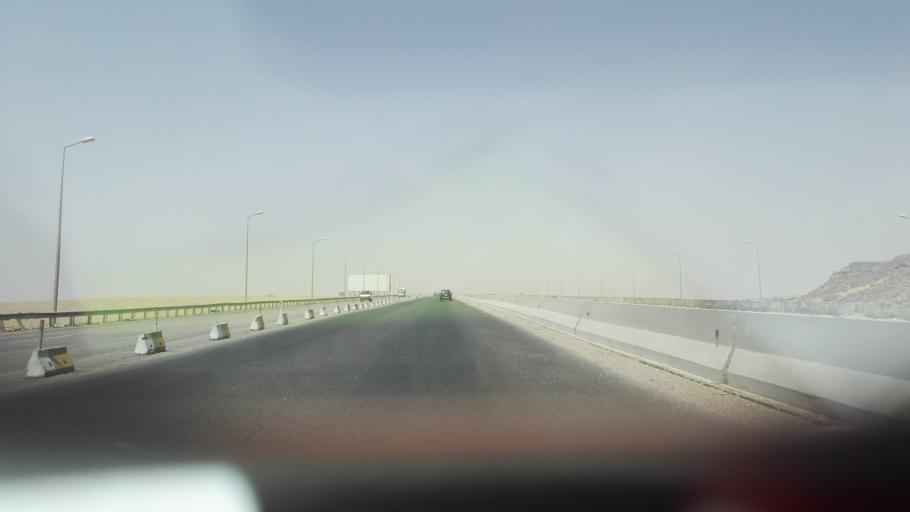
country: EG
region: As Suways
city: Ain Sukhna
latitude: 29.7120
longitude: 32.0751
